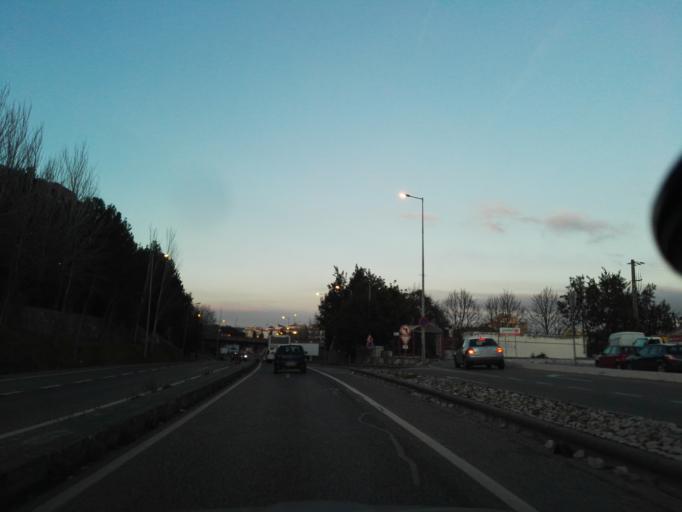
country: PT
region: Lisbon
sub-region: Vila Franca de Xira
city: Vialonga
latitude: 38.8890
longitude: -9.0443
